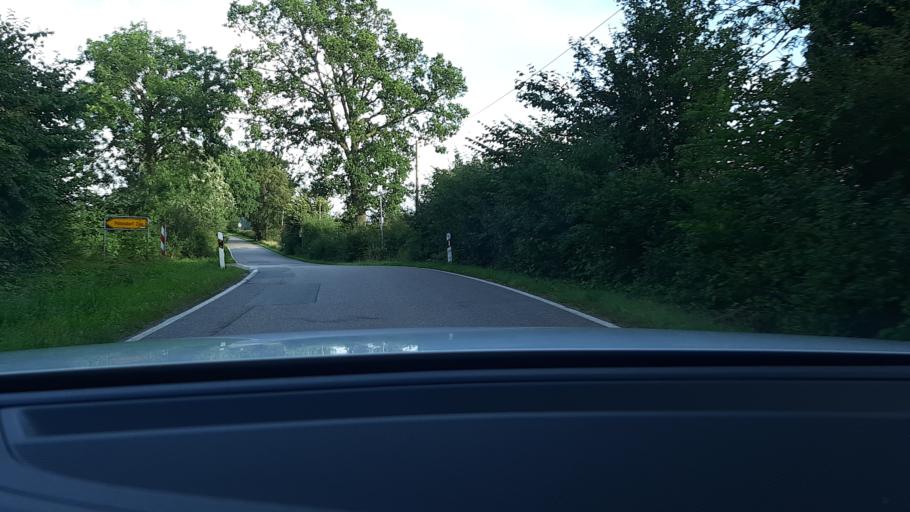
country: DE
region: Schleswig-Holstein
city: Stockelsdorf
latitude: 53.9229
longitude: 10.6151
